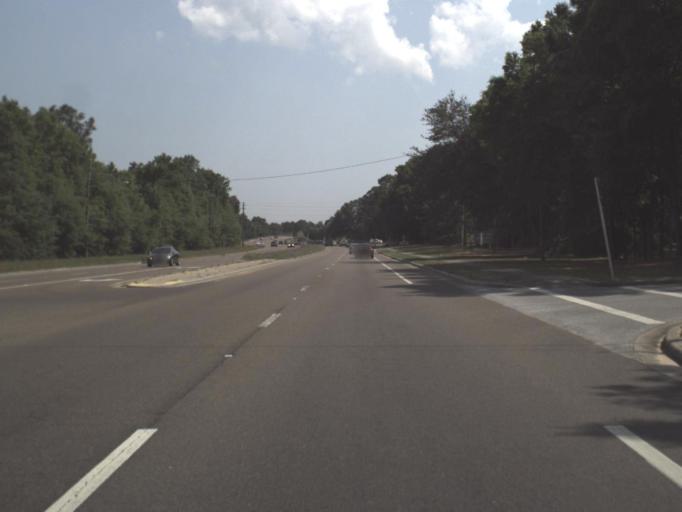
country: US
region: Florida
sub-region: Escambia County
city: Ferry Pass
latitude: 30.5087
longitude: -87.1846
